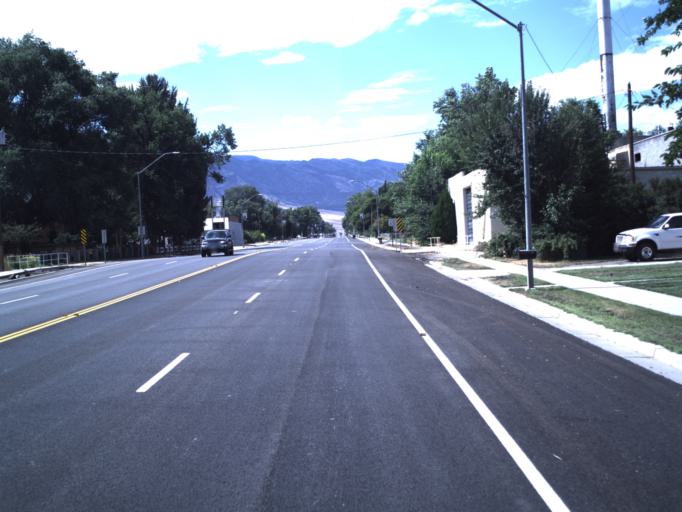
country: US
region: Utah
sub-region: Sevier County
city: Monroe
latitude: 38.6385
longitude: -112.1215
